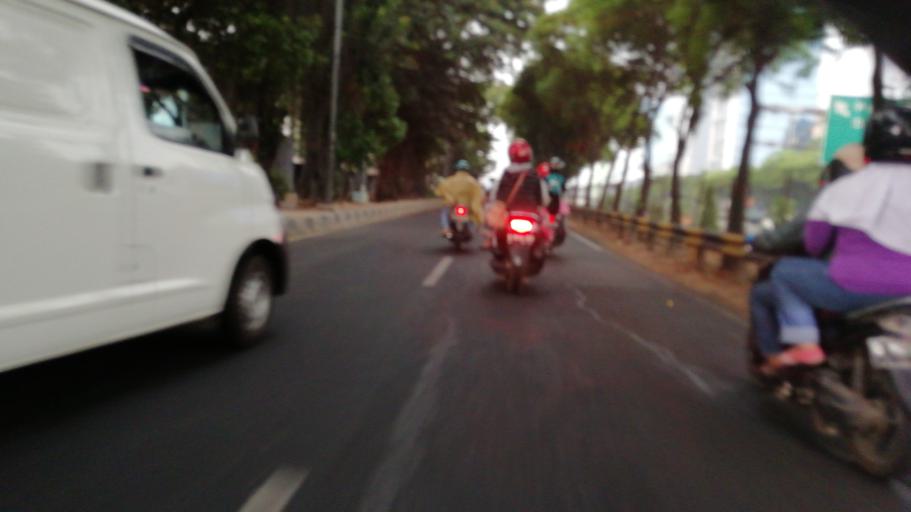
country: ID
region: Jakarta Raya
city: Jakarta
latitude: -6.2981
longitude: 106.8314
